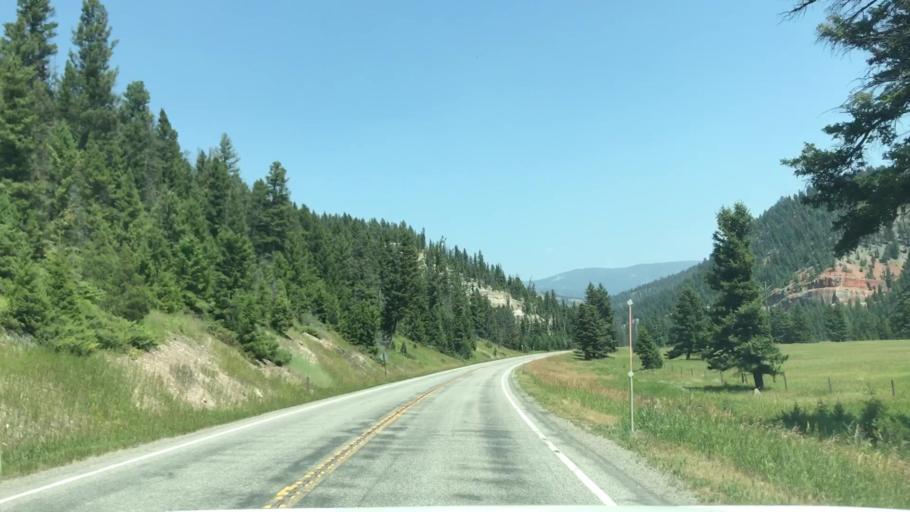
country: US
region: Montana
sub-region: Gallatin County
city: Big Sky
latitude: 45.1636
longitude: -111.2483
